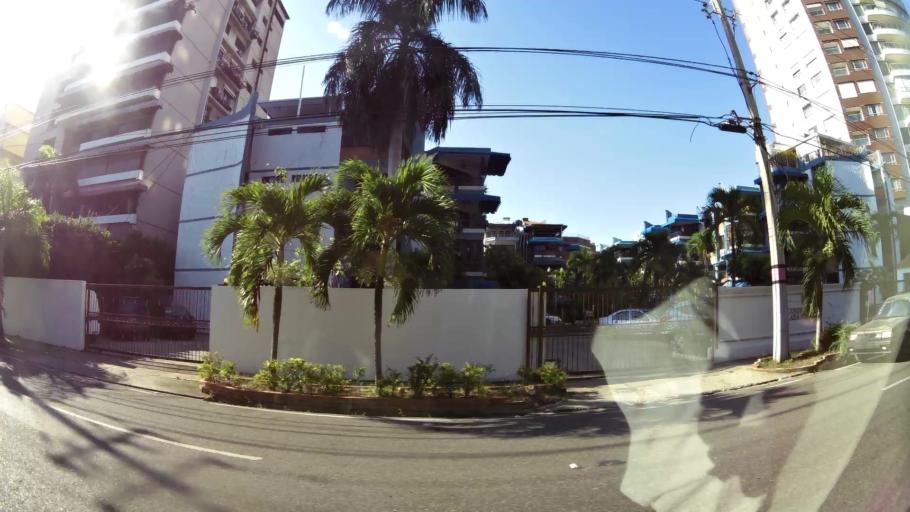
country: DO
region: Nacional
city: Bella Vista
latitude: 18.4473
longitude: -69.9458
